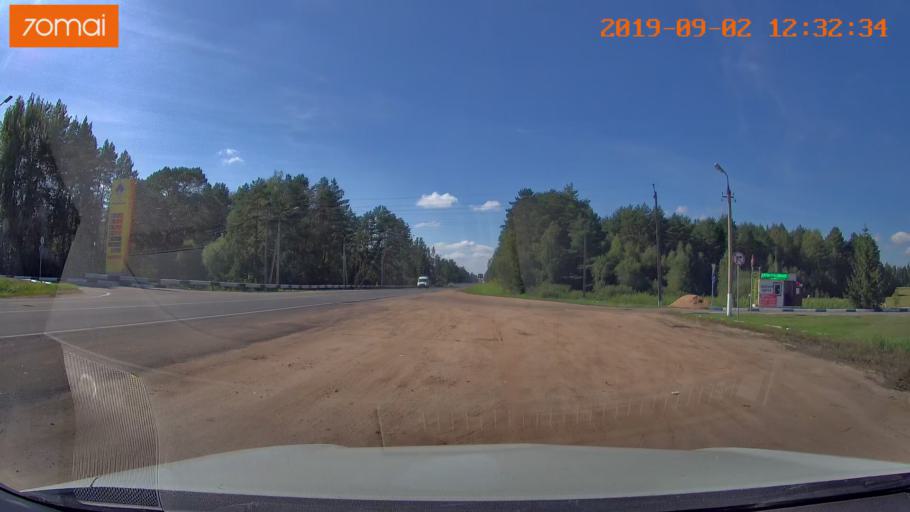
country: RU
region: Smolensk
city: Shumyachi
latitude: 53.8226
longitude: 32.4435
